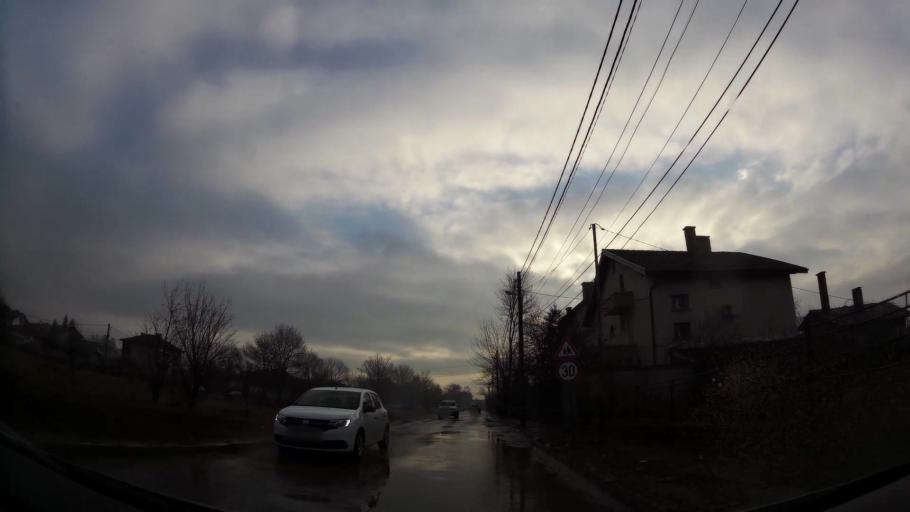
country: BG
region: Sofia-Capital
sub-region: Stolichna Obshtina
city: Sofia
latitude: 42.7374
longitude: 23.3375
